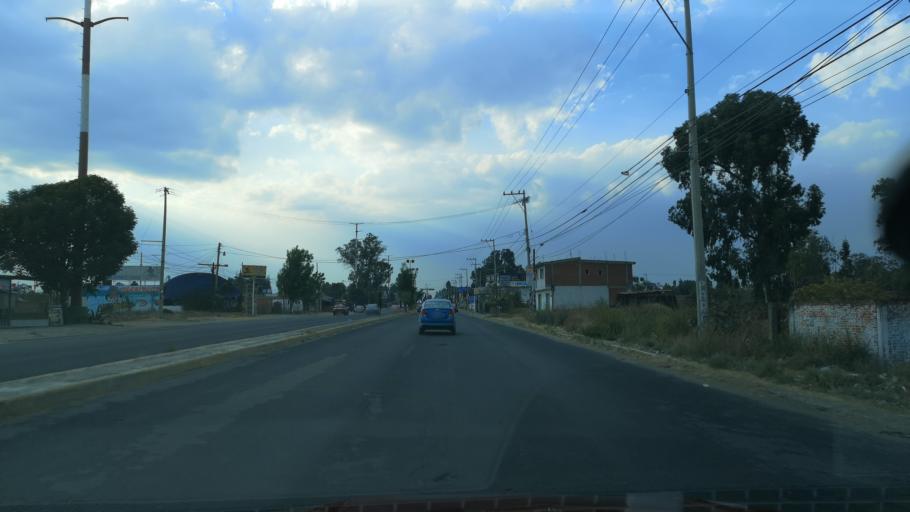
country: MX
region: Puebla
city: Cuanala
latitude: 19.1001
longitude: -98.3448
